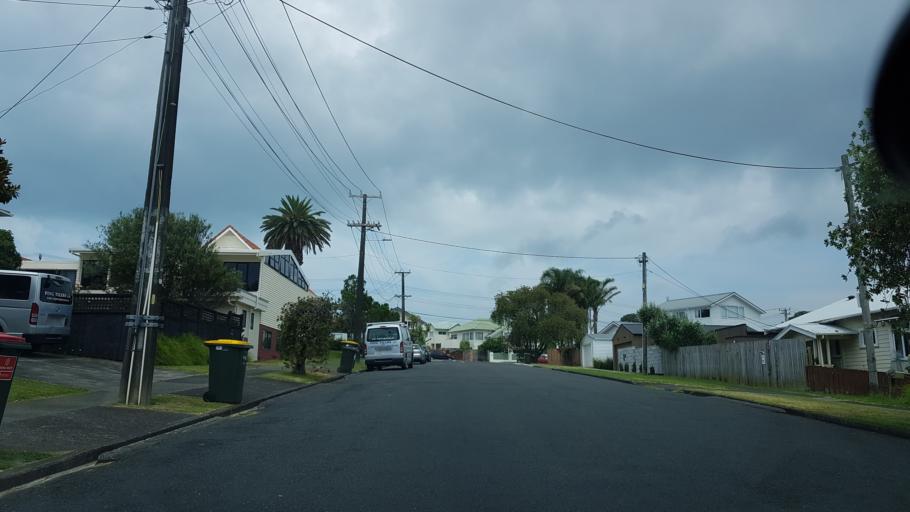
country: NZ
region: Auckland
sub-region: Auckland
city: North Shore
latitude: -36.7982
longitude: 174.7772
